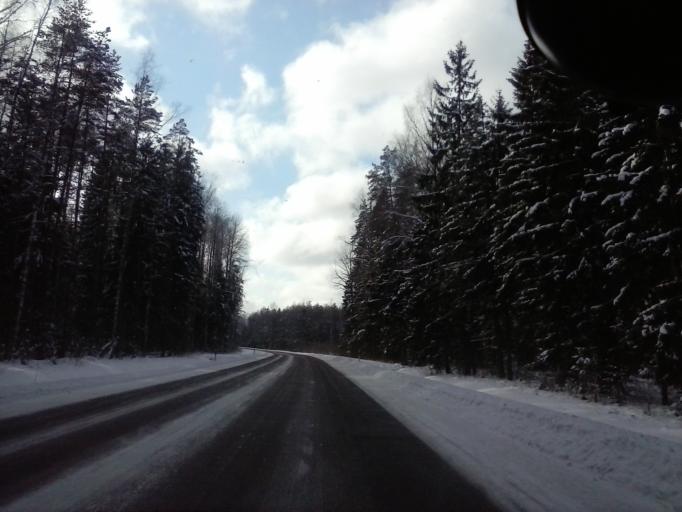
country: EE
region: Viljandimaa
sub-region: Moisakuela linn
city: Moisakula
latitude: 58.2420
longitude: 25.1291
